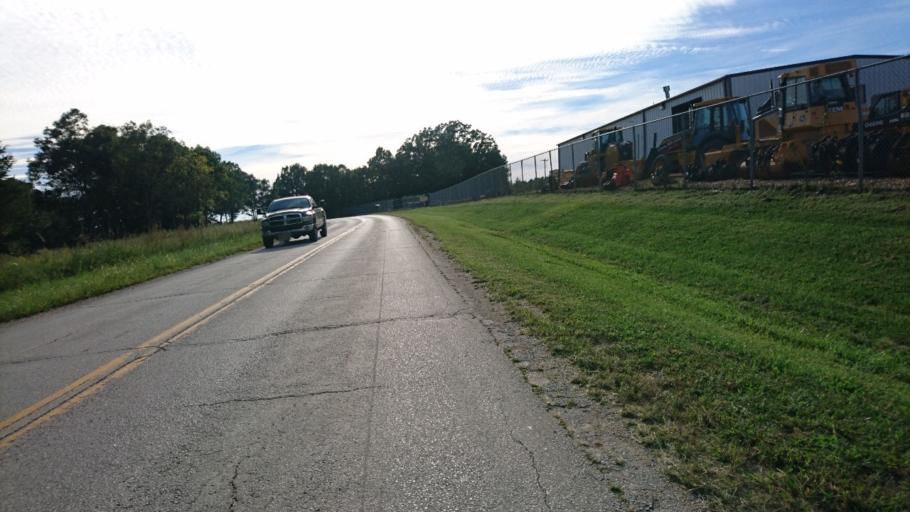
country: US
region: Missouri
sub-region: Crawford County
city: Cuba
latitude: 38.0958
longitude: -91.3621
